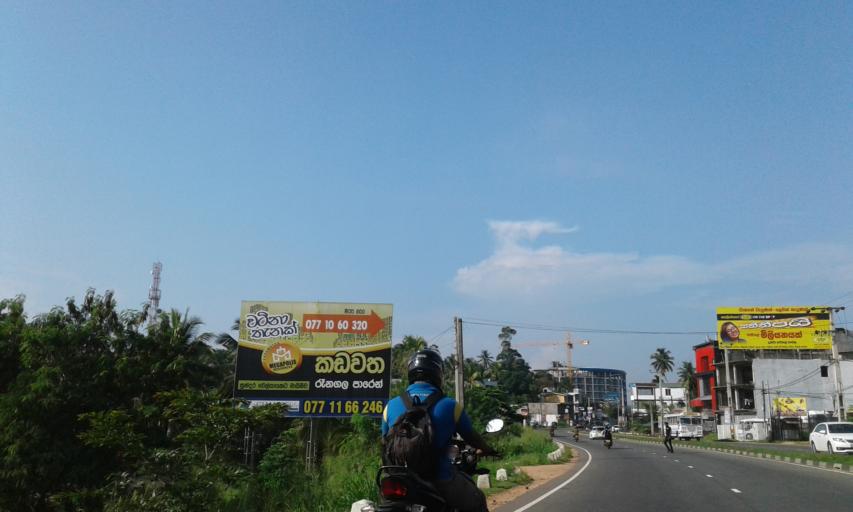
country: LK
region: Western
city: Gampaha
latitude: 7.0334
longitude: 79.9886
